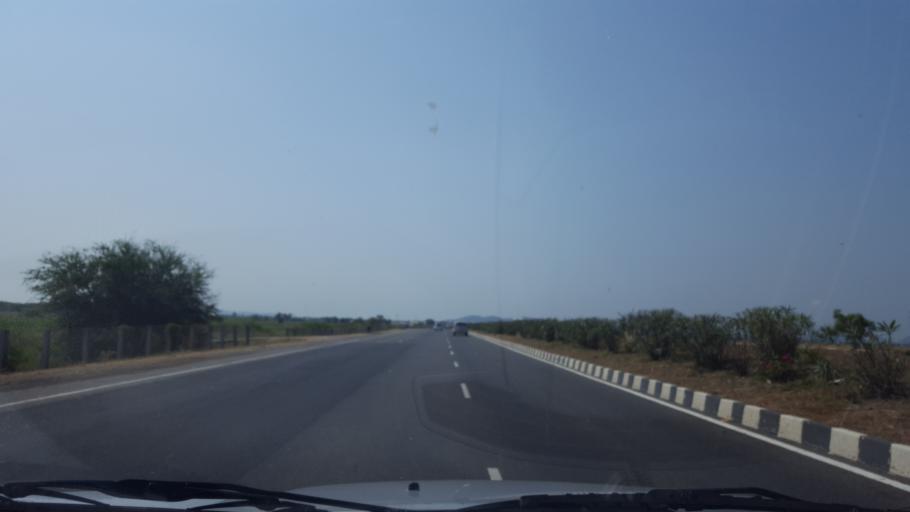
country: IN
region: Andhra Pradesh
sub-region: Guntur
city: Chilakalurupet
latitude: 16.0205
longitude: 80.1235
